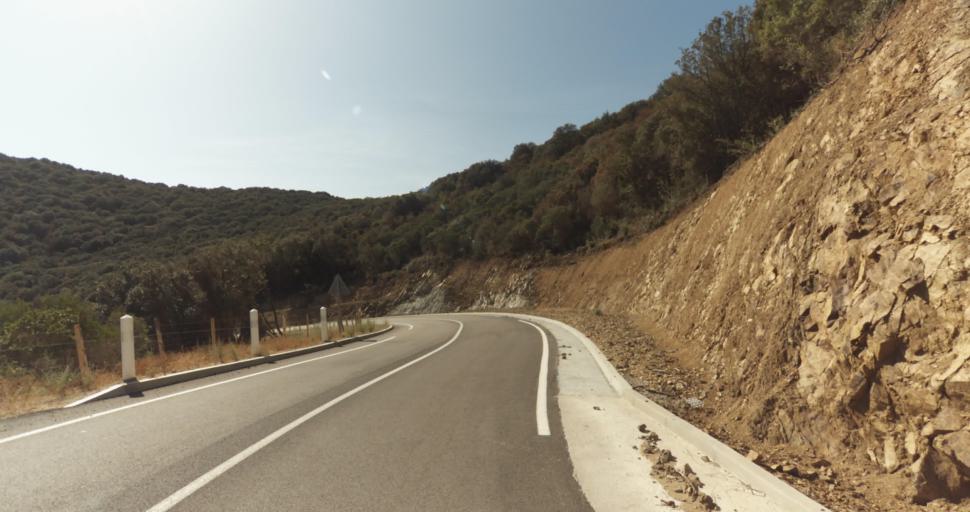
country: FR
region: Corsica
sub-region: Departement de la Corse-du-Sud
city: Ajaccio
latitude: 41.9249
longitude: 8.6455
